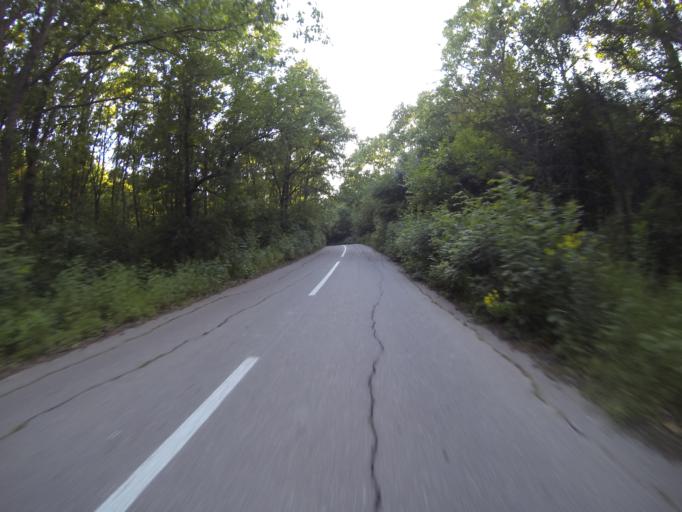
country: RO
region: Dolj
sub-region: Comuna Tuglui
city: Tuglui
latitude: 44.1623
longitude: 23.8141
